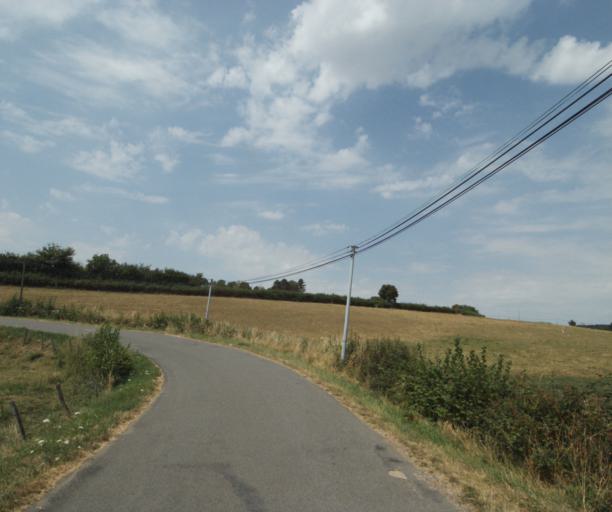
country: FR
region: Bourgogne
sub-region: Departement de Saone-et-Loire
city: Gueugnon
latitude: 46.5975
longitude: 4.0265
